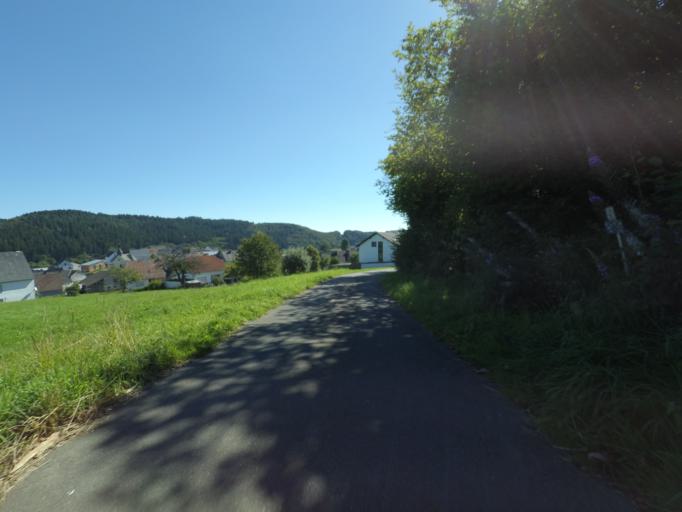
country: DE
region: Rheinland-Pfalz
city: Utzerath
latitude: 50.2218
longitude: 6.9326
